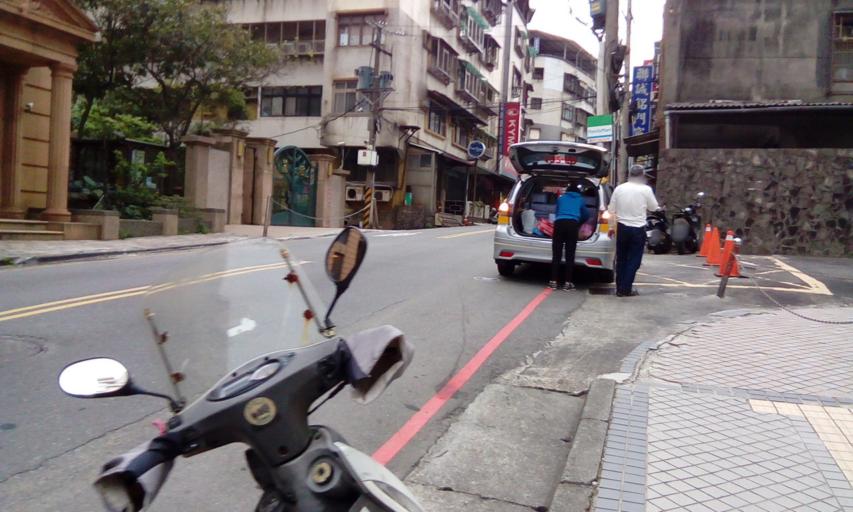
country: TW
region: Taipei
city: Taipei
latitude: 25.1759
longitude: 121.4390
